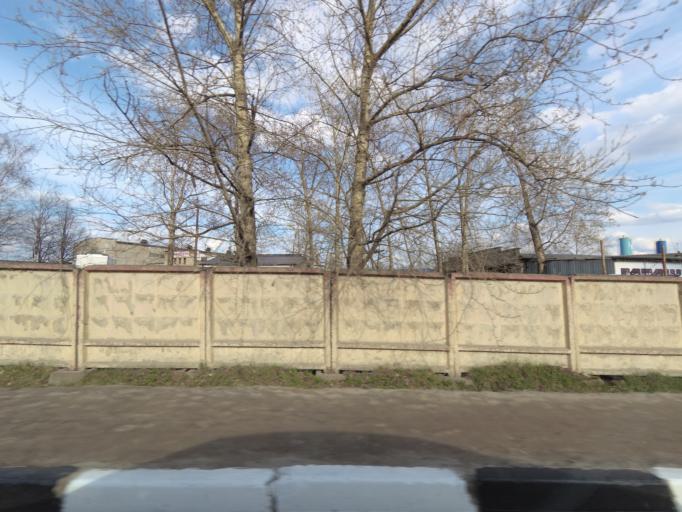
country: RU
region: Moskovskaya
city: Lobnya
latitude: 56.0133
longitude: 37.4374
